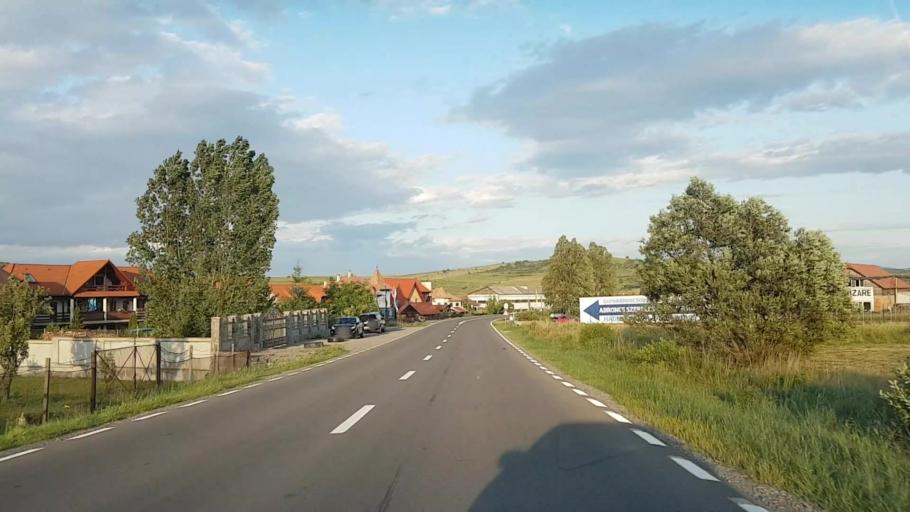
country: RO
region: Harghita
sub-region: Comuna Lupeni
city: Lupeni
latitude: 46.3706
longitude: 25.2273
